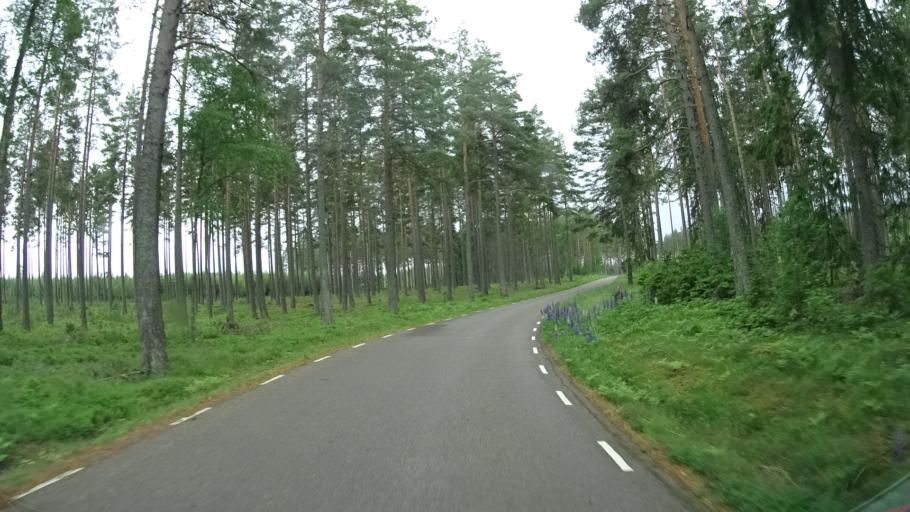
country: SE
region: Kalmar
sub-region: Vimmerby Kommun
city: Sodra Vi
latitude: 57.7147
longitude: 15.7718
